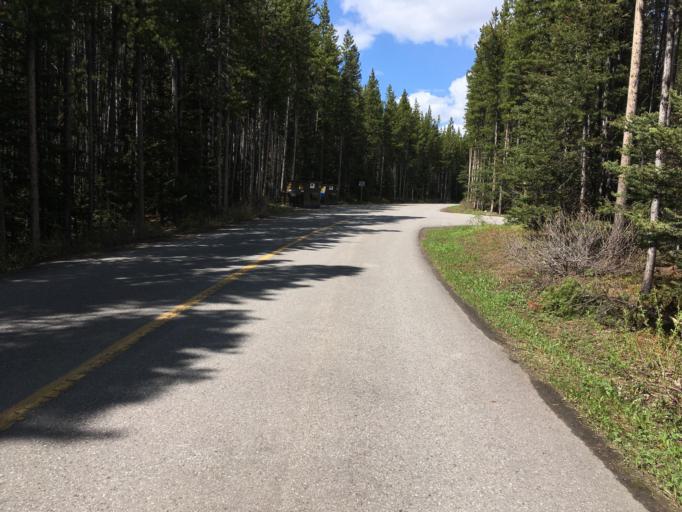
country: CA
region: Alberta
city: Canmore
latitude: 50.6291
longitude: -115.0998
